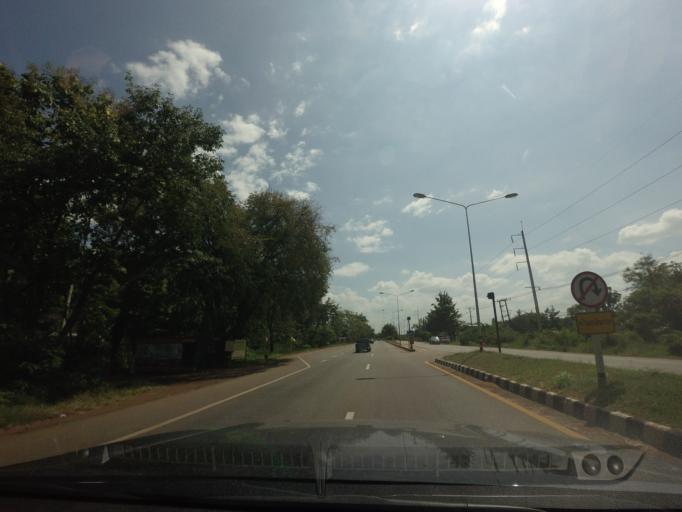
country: TH
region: Phetchabun
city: Nong Phai
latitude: 15.9278
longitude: 101.0262
